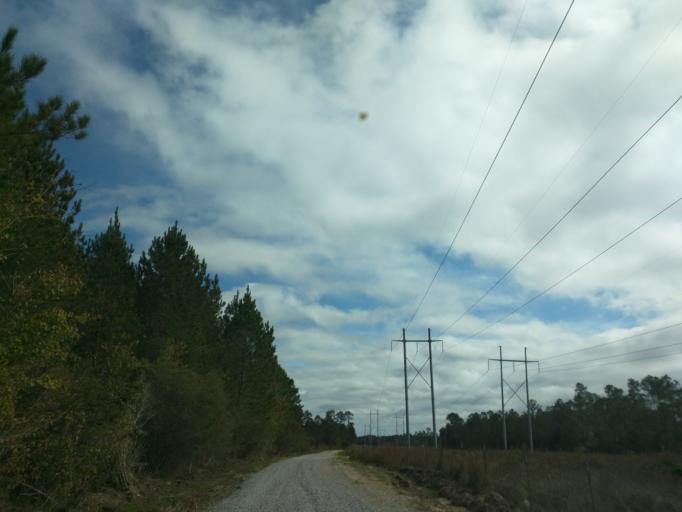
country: US
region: Florida
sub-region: Escambia County
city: Cantonment
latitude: 30.5332
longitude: -87.4350
